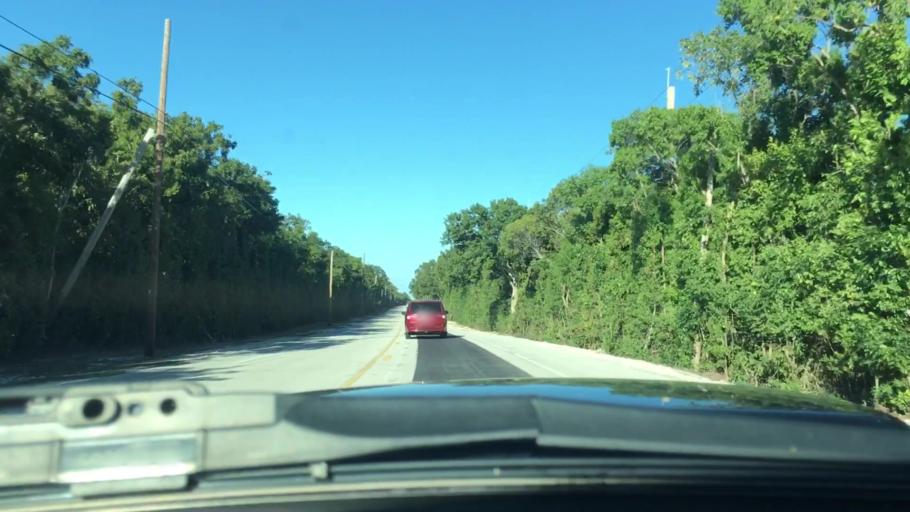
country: US
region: Florida
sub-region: Monroe County
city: North Key Largo
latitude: 25.2064
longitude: -80.3432
